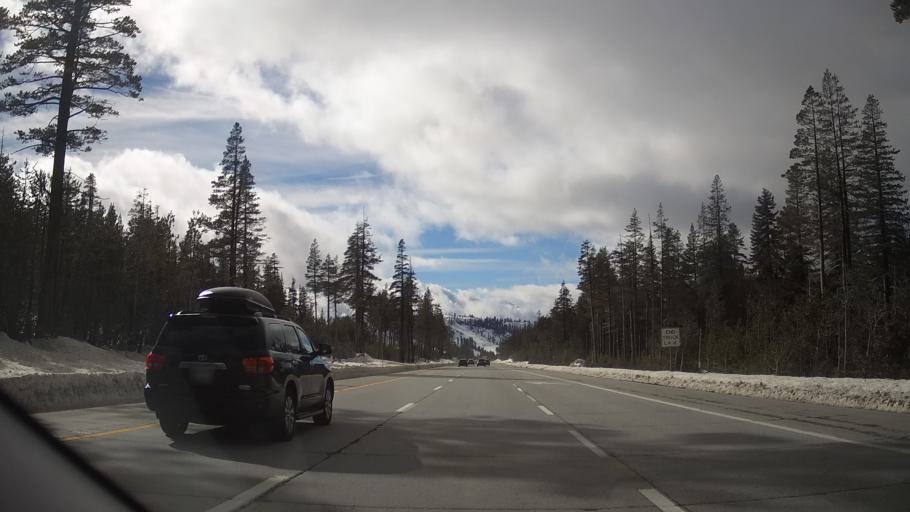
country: US
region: California
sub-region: Nevada County
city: Truckee
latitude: 39.3331
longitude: -120.3600
